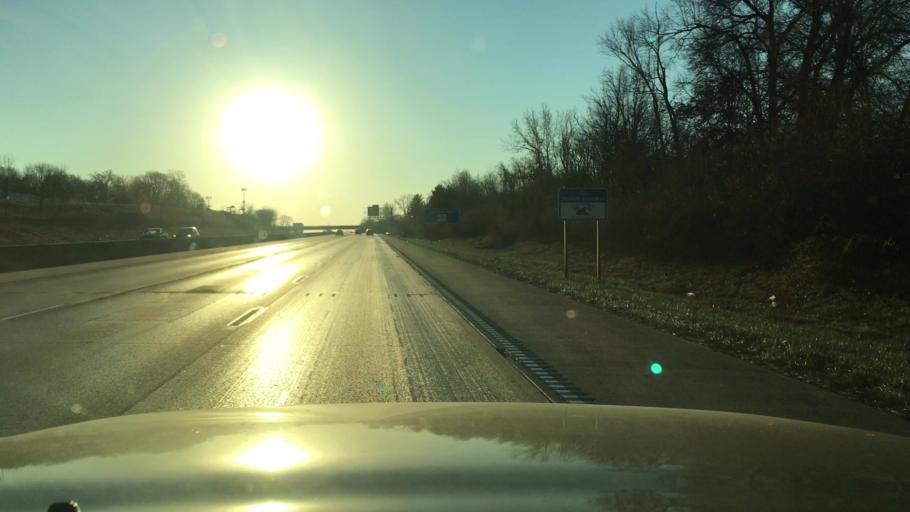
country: US
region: Missouri
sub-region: Saint Charles County
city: Saint Charles
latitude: 38.8106
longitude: -90.4871
